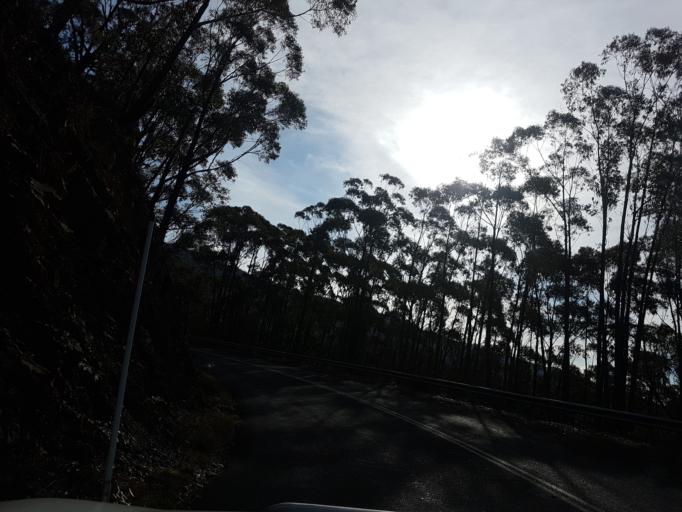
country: AU
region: Victoria
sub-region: Latrobe
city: Moe
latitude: -37.8540
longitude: 146.3962
